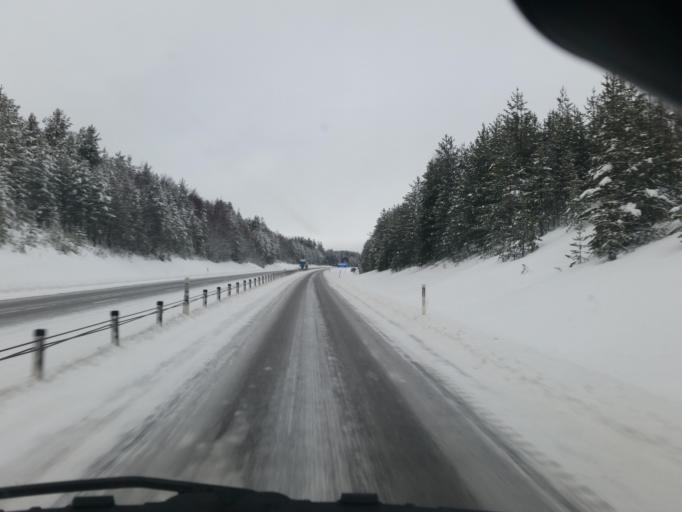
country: SE
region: Norrbotten
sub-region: Pitea Kommun
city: Bergsviken
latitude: 65.3007
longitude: 21.4153
